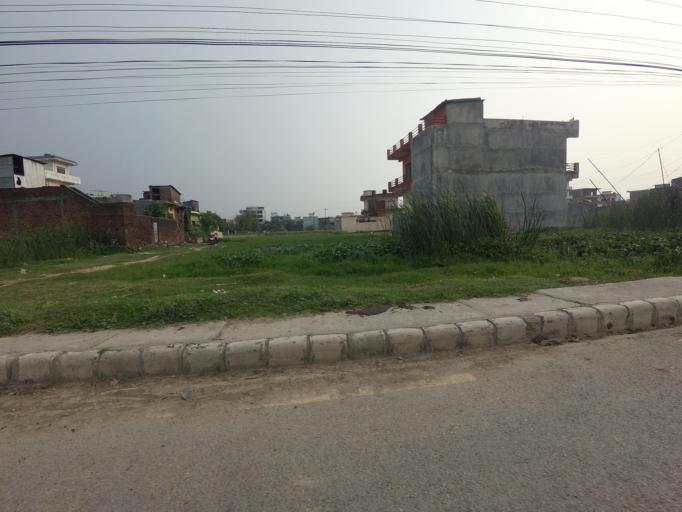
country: NP
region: Western Region
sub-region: Lumbini Zone
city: Bhairahawa
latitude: 27.5050
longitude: 83.4461
